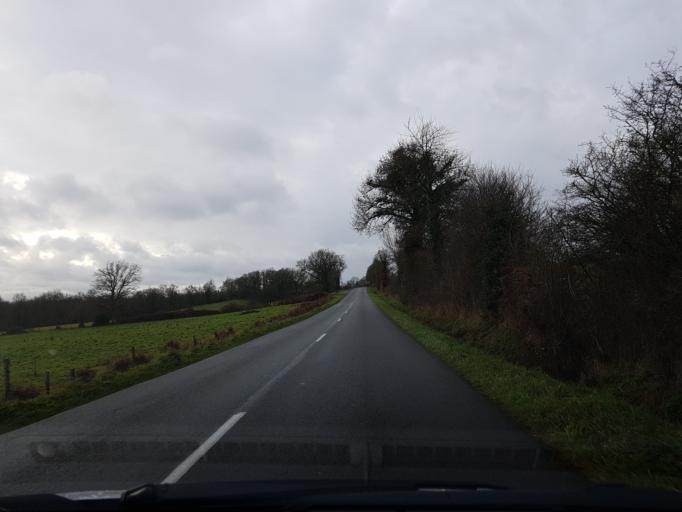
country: FR
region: Poitou-Charentes
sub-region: Departement de la Charente
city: Chabanais
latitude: 45.9022
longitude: 0.7321
